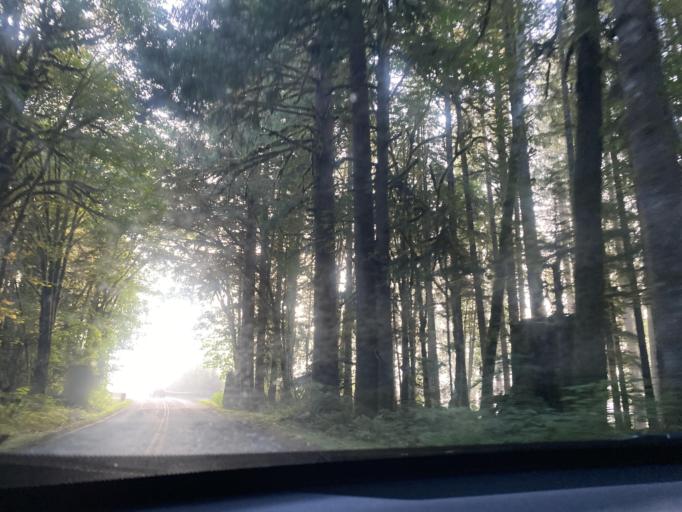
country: US
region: Washington
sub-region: Clallam County
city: Forks
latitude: 47.8100
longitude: -124.0821
